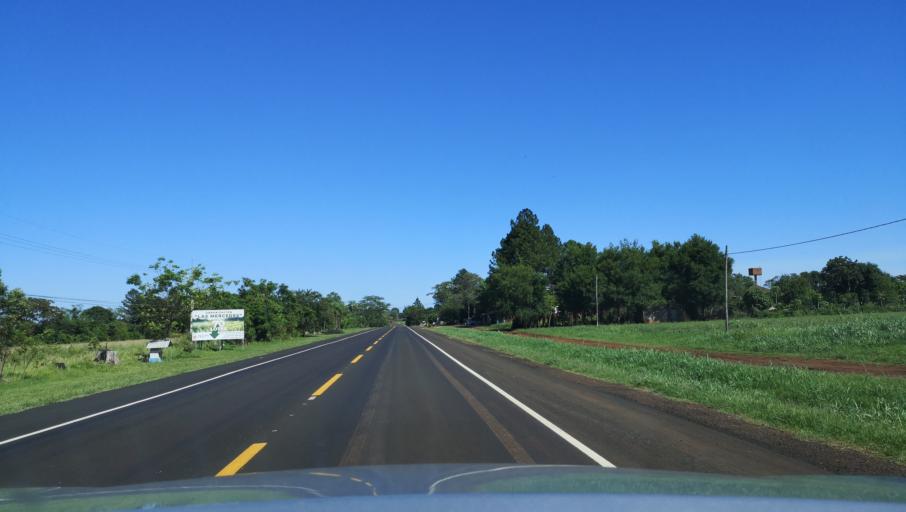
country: PY
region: Itapua
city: San Juan del Parana
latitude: -27.2638
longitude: -55.9618
